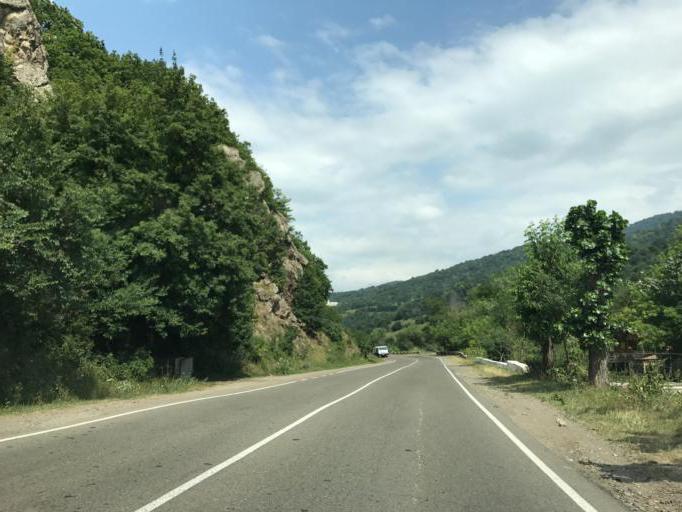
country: AM
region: Tavush
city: Dilijan
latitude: 40.7602
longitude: 44.9060
